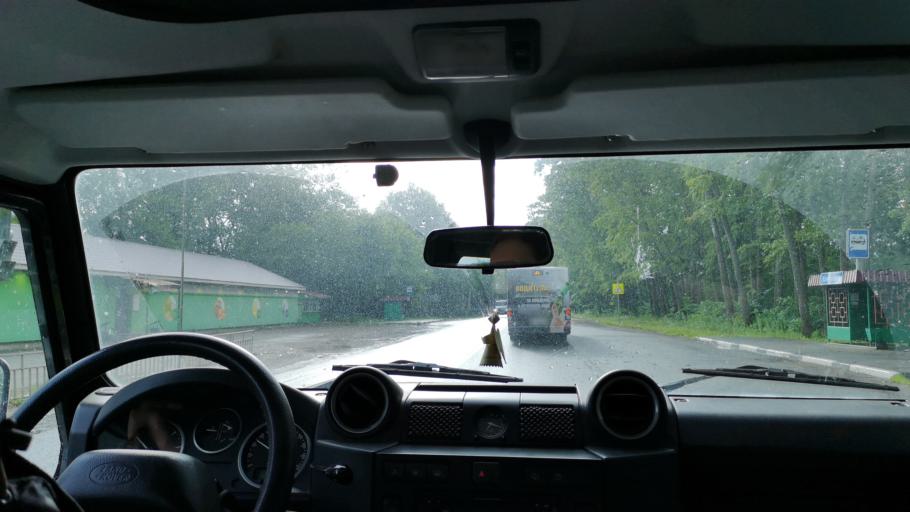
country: RU
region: Moskovskaya
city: Gorshkovo
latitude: 56.3678
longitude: 37.4563
